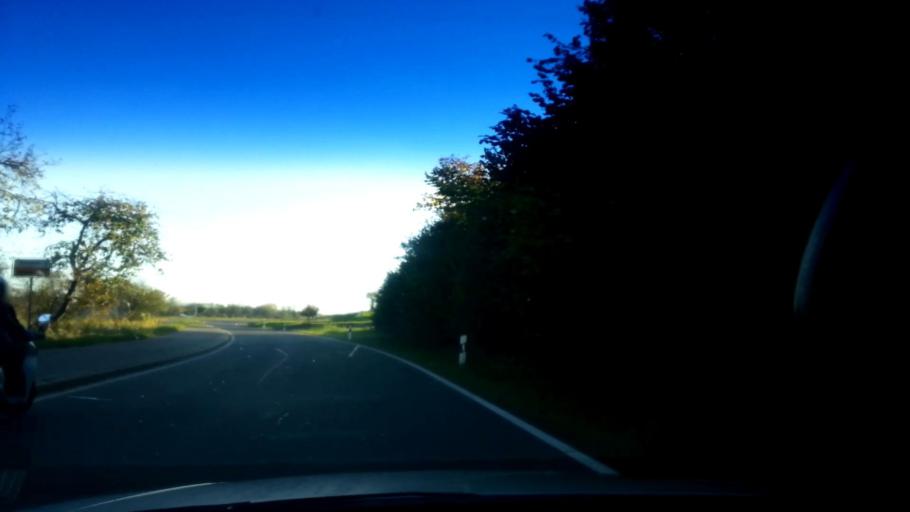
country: DE
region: Bavaria
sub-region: Upper Franconia
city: Rattelsdorf
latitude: 50.0025
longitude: 10.8725
